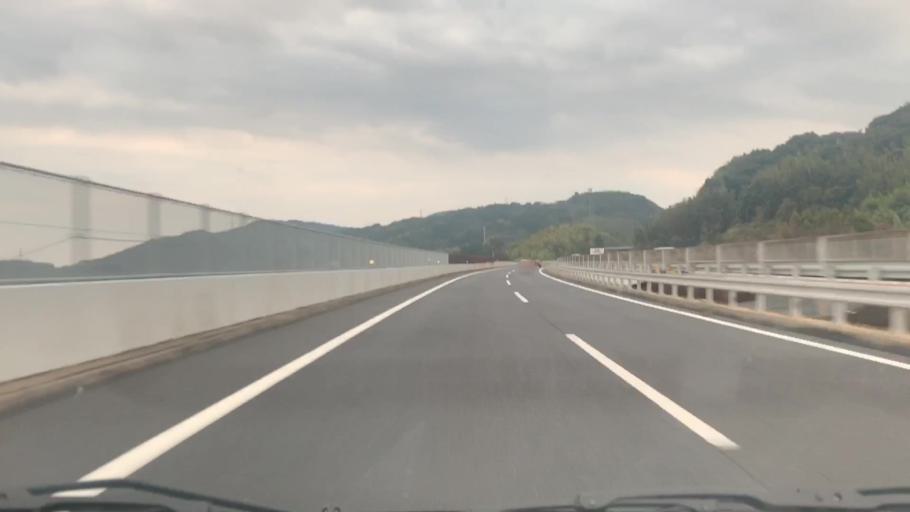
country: JP
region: Nagasaki
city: Omura
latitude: 32.8887
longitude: 129.9918
